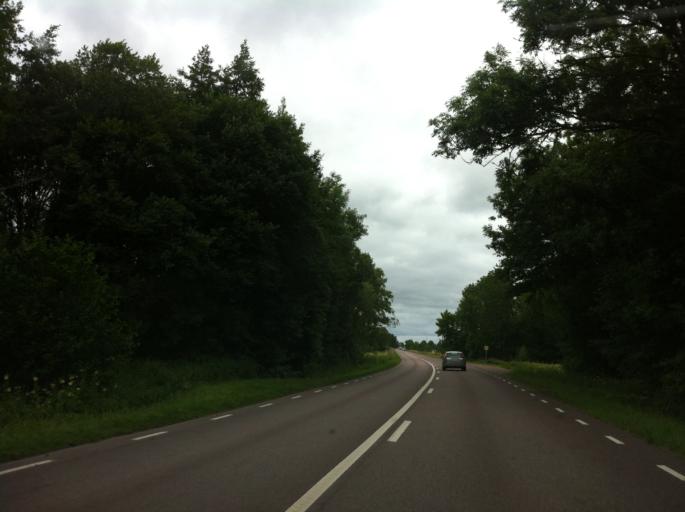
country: SE
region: Kalmar
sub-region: Borgholms Kommun
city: Borgholm
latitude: 57.2017
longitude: 17.0454
